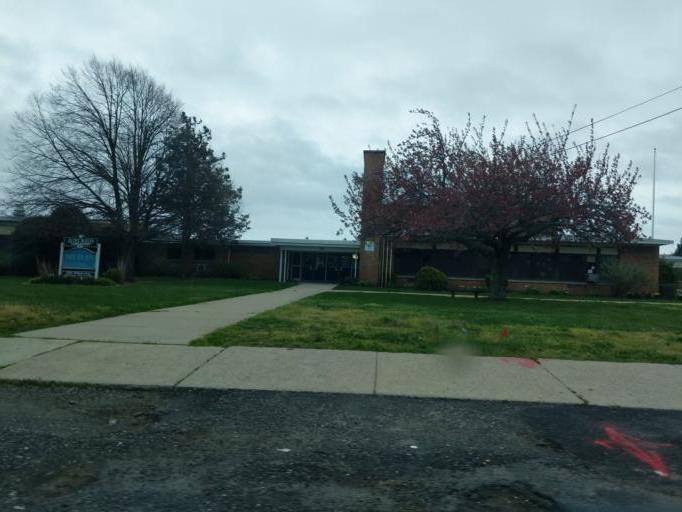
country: US
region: New York
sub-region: Nassau County
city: Baldwin
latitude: 40.6490
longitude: -73.6051
